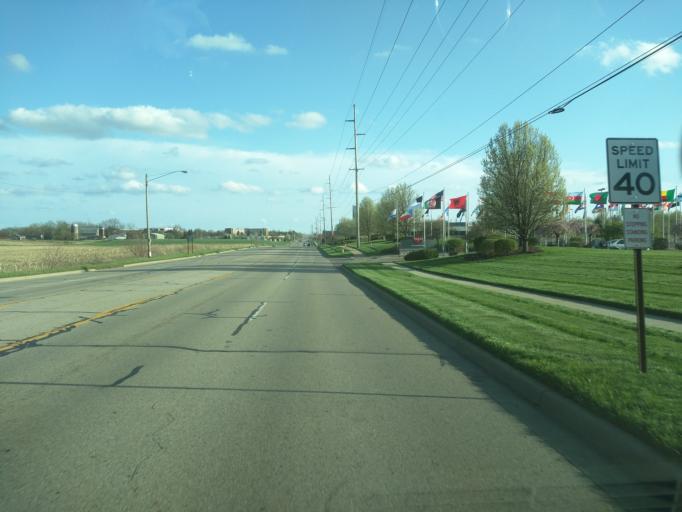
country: US
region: Michigan
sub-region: Eaton County
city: Waverly
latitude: 42.7330
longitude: -84.6423
